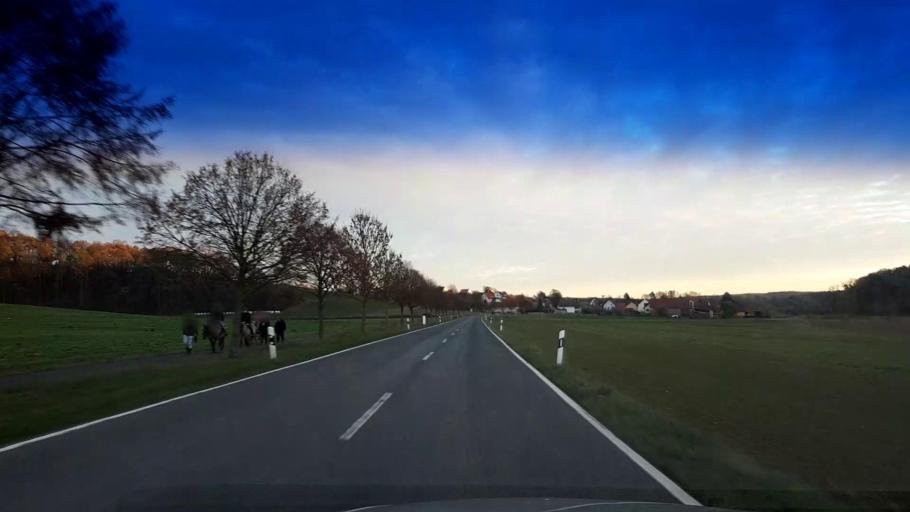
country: DE
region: Bavaria
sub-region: Upper Franconia
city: Walsdorf
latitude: 49.8858
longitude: 10.7537
